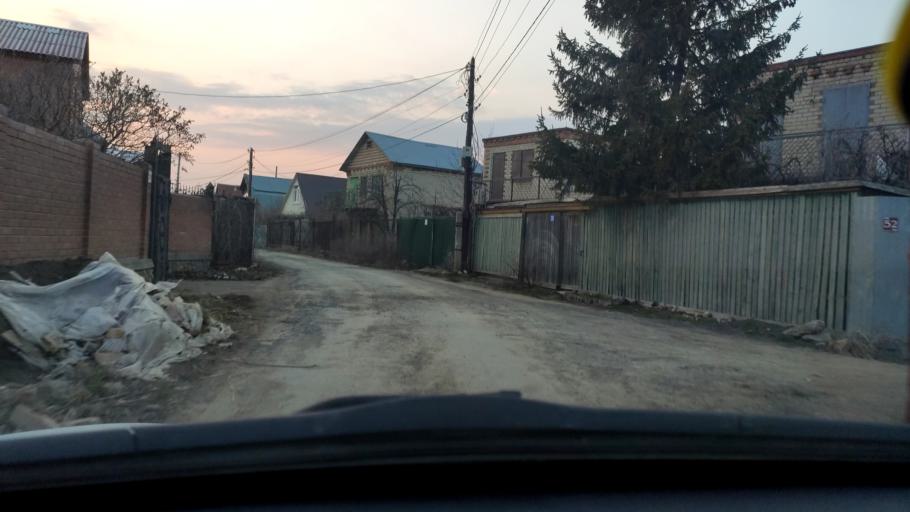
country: RU
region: Samara
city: Zhigulevsk
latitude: 53.4519
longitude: 49.5228
